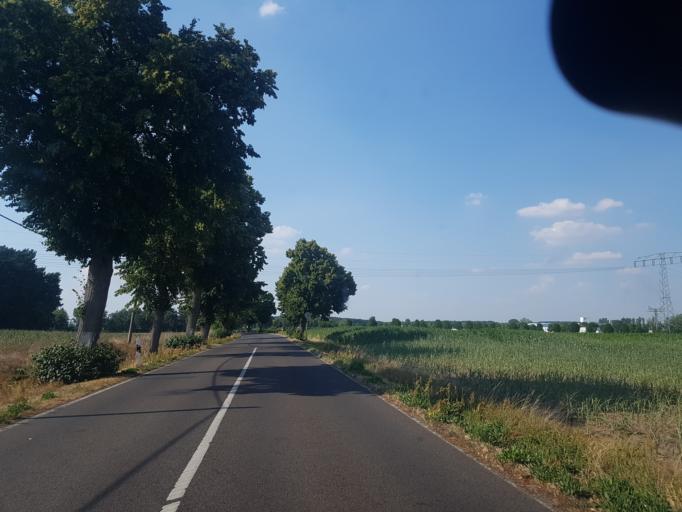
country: DE
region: Brandenburg
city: Trebbin
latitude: 52.1822
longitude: 13.2355
